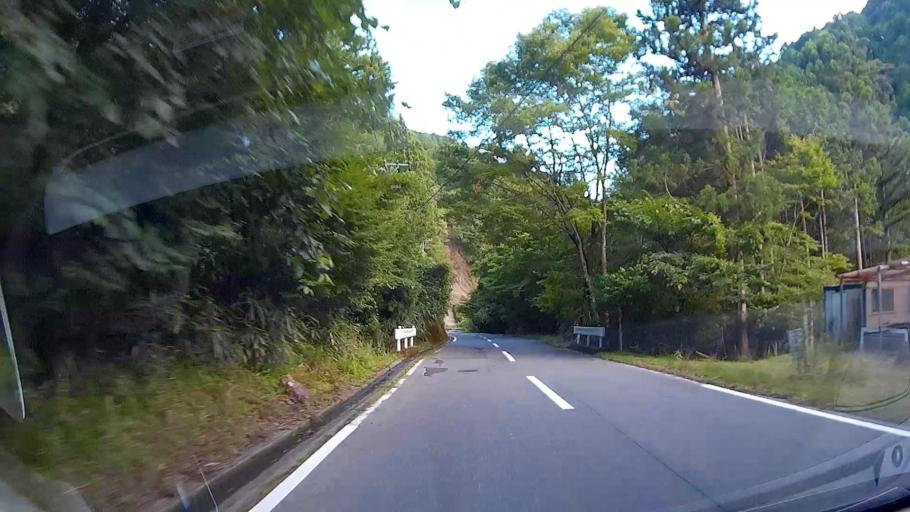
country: JP
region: Shizuoka
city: Shizuoka-shi
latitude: 35.1479
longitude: 138.2670
